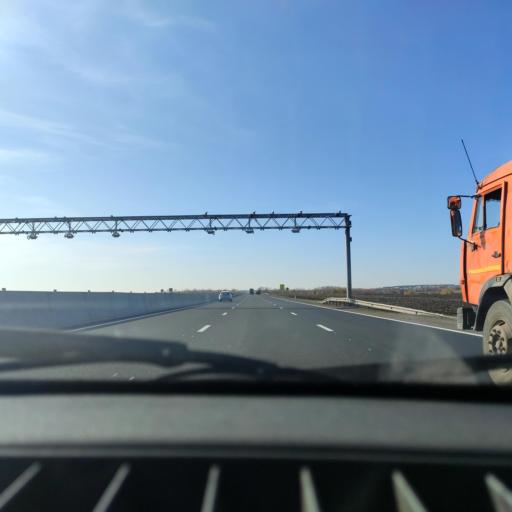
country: RU
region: Bashkortostan
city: Avdon
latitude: 54.6734
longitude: 55.7791
